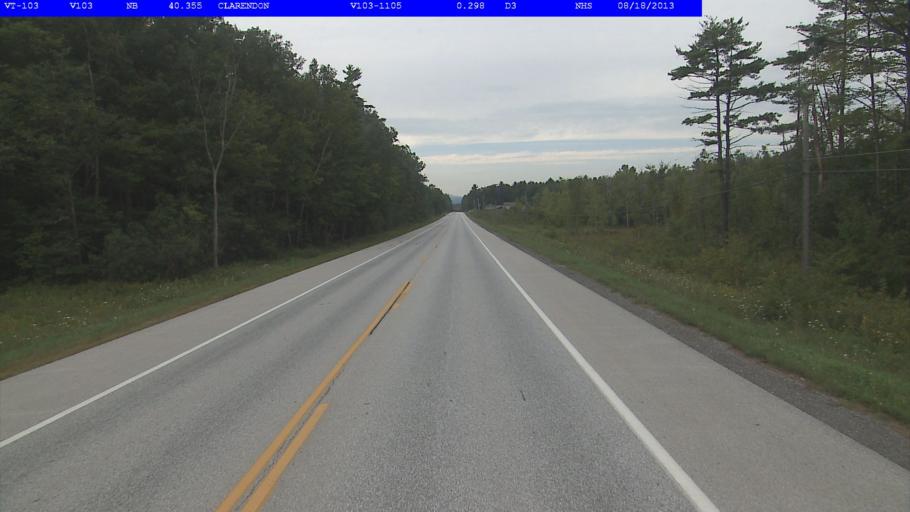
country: US
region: Vermont
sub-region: Rutland County
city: Rutland
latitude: 43.5273
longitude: -72.9342
